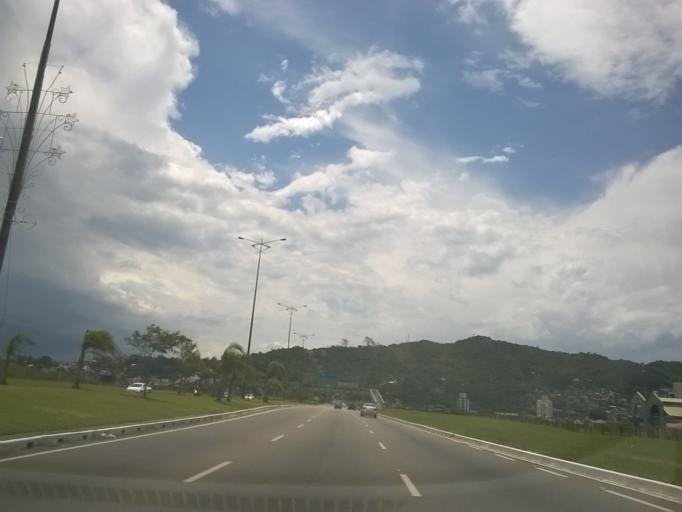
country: BR
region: Santa Catarina
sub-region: Florianopolis
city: Saco dos Limoes
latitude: -27.6133
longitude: -48.5312
